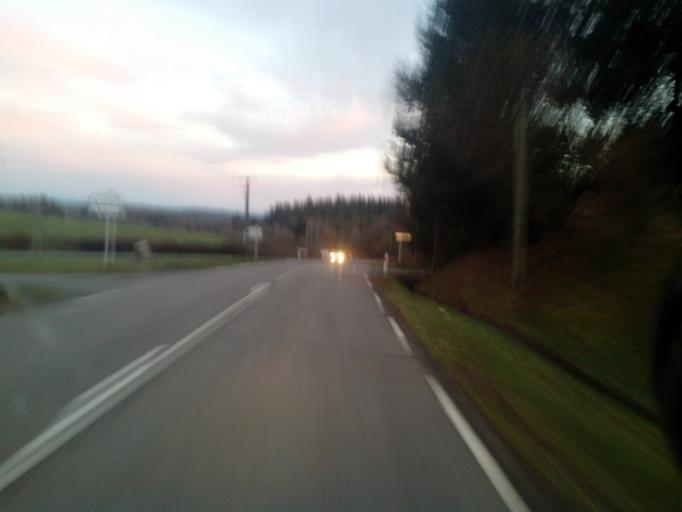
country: FR
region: Limousin
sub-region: Departement de la Correze
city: Meymac
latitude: 45.5174
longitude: 2.1744
